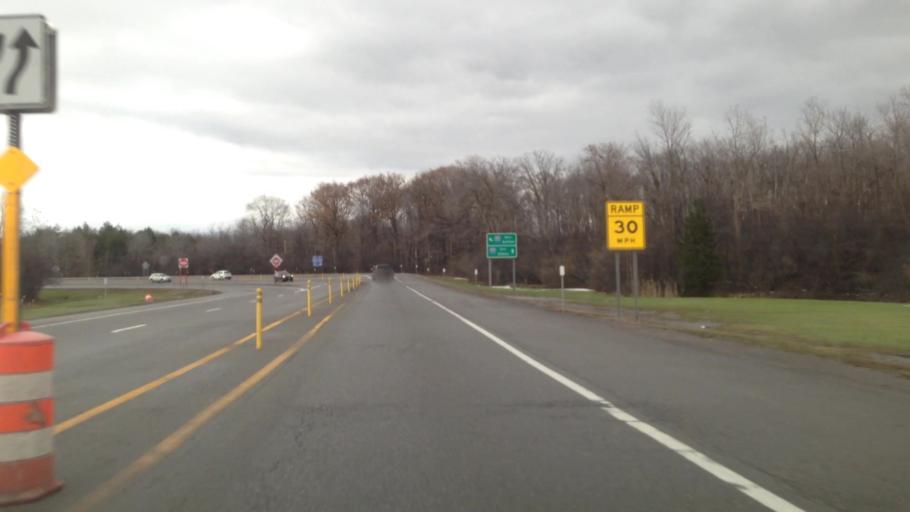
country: US
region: New York
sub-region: Genesee County
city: Batavia
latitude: 43.0161
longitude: -78.1885
